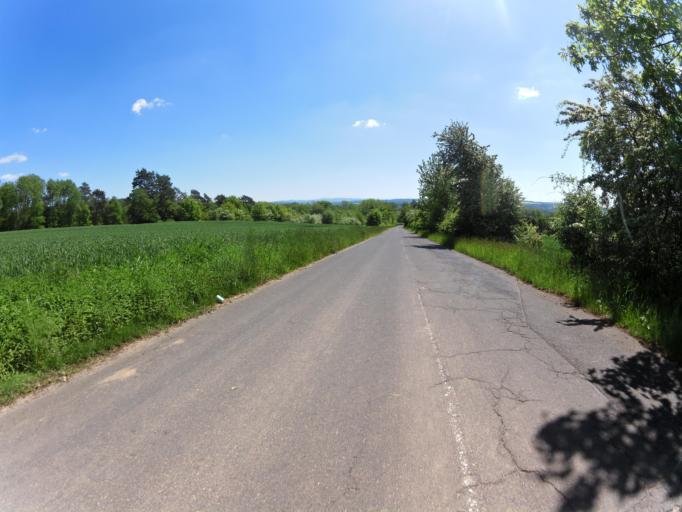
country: DE
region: Thuringia
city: Dankmarshausen
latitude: 50.9571
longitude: 10.0117
